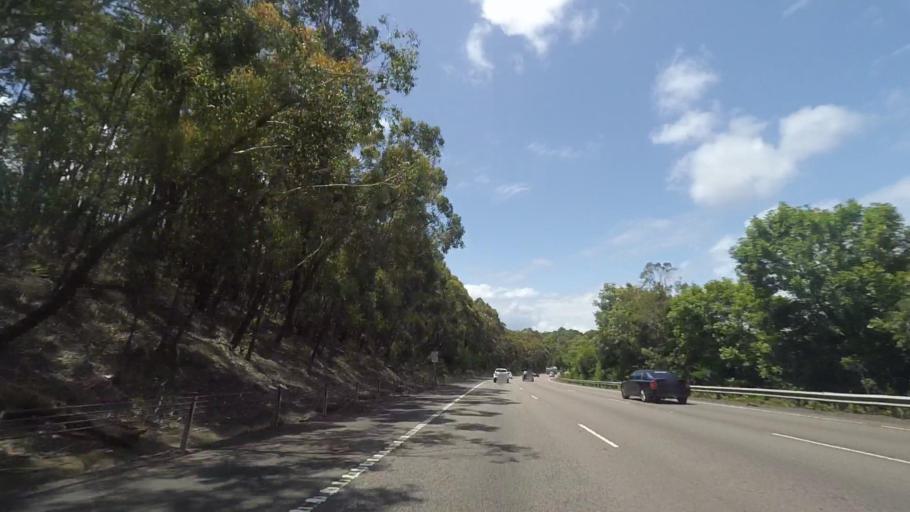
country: AU
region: New South Wales
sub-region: Gosford Shire
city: Lisarow
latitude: -33.3630
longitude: 151.3335
